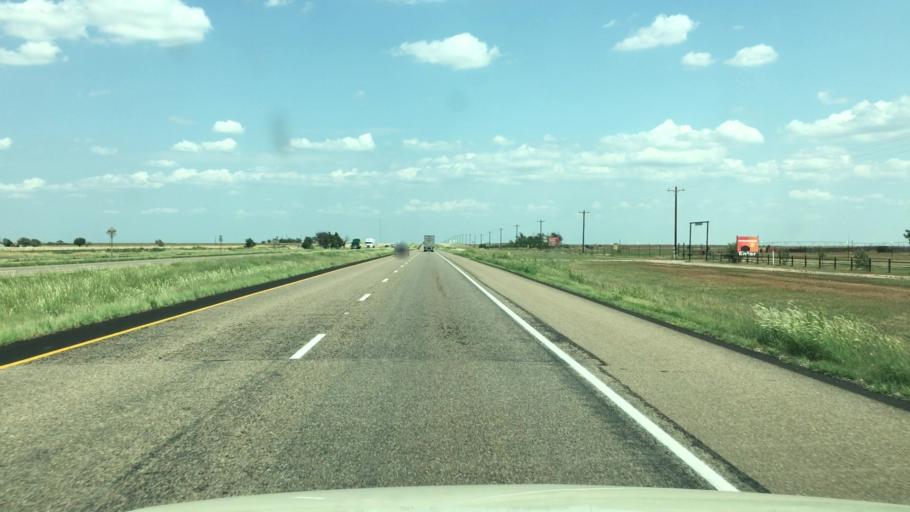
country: US
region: Texas
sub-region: Armstrong County
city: Claude
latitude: 35.0338
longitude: -101.1821
